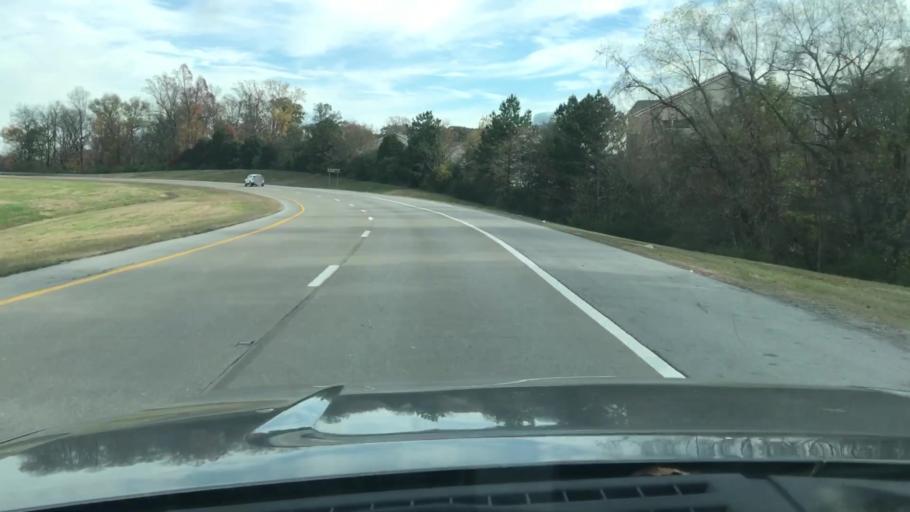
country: US
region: Tennessee
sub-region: Davidson County
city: Lakewood
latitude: 36.1672
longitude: -86.6087
